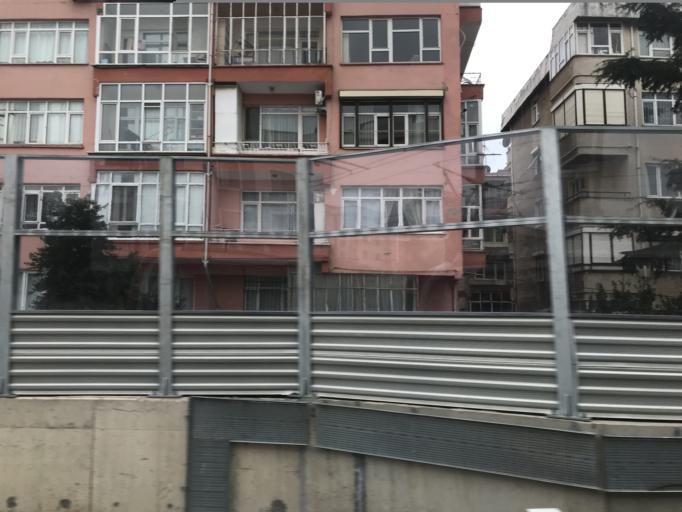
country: TR
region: Istanbul
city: Pendik
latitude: 40.8806
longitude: 29.2233
